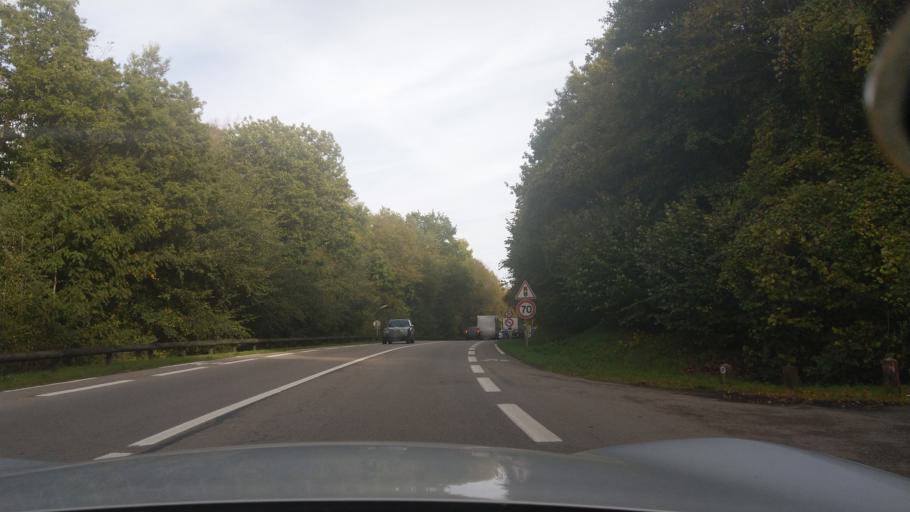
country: FR
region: Ile-de-France
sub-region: Departement des Yvelines
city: Acheres
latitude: 48.9394
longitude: 2.0735
